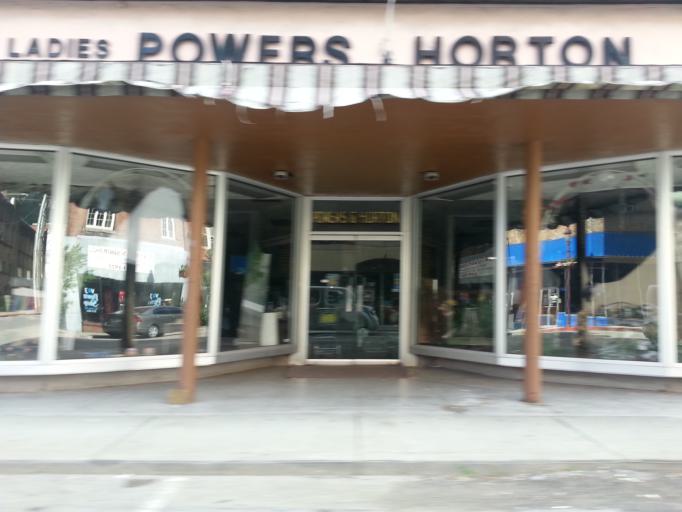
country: US
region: Kentucky
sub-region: Harlan County
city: Harlan
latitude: 36.8463
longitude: -83.3229
